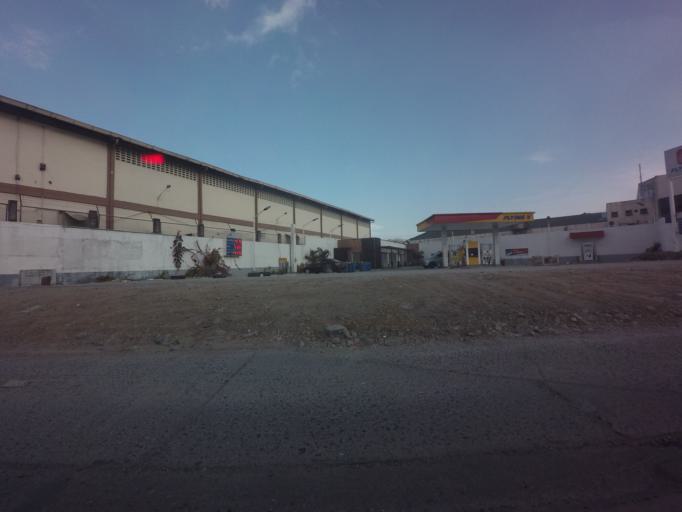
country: PH
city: Sambayanihan People's Village
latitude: 14.4972
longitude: 121.0020
